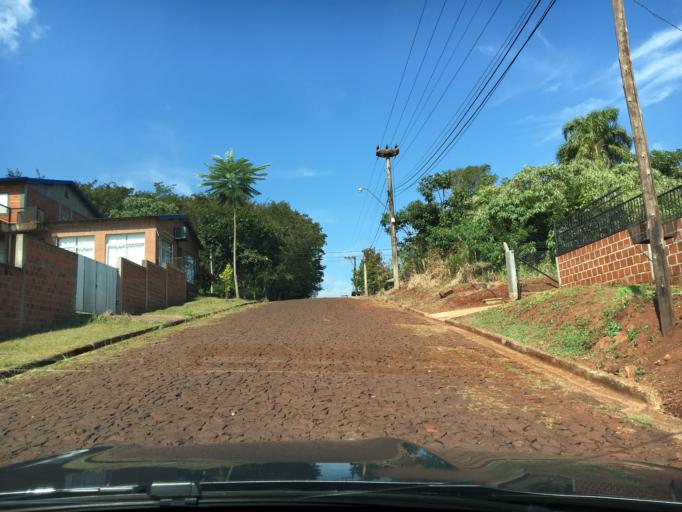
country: AR
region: Misiones
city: Puerto Rico
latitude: -26.8184
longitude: -55.0361
